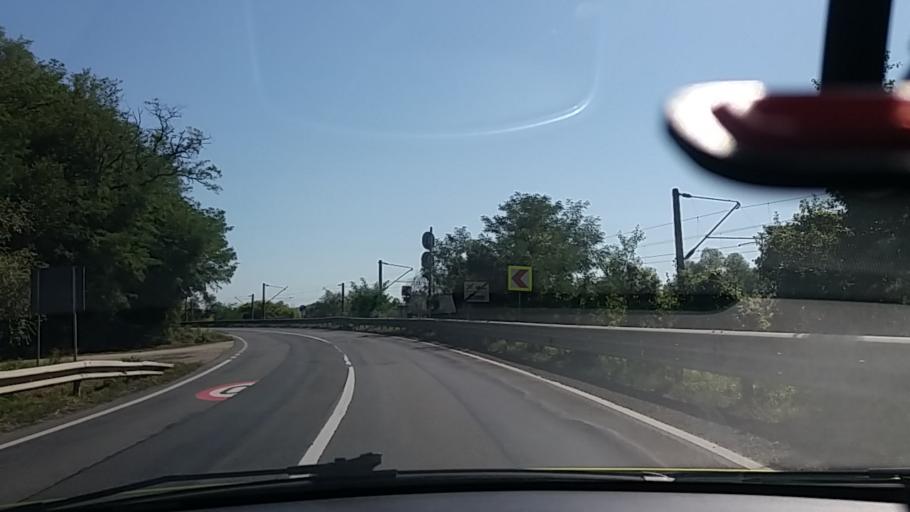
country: RO
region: Arad
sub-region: Comuna Conop
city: Conop
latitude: 46.0994
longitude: 21.8792
